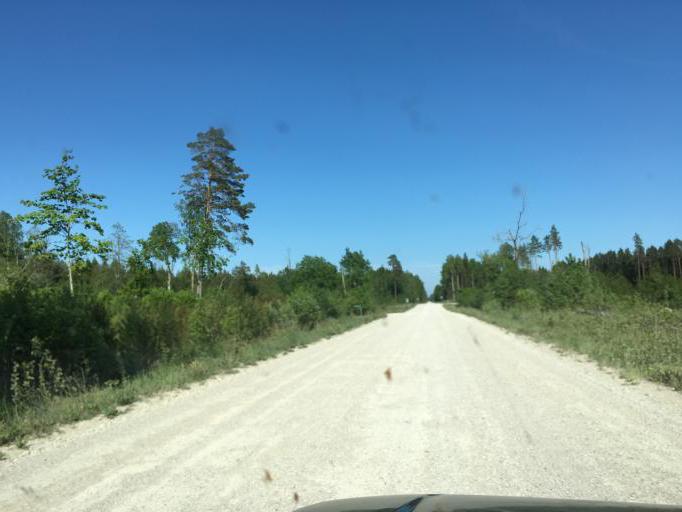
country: LV
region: Dundaga
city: Dundaga
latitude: 57.6135
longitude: 22.4995
